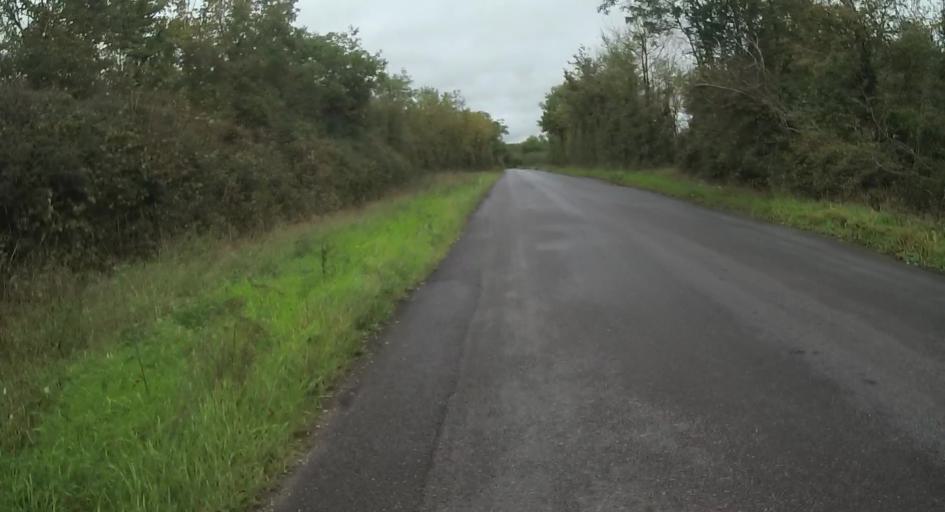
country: GB
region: England
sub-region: Hampshire
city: Tadley
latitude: 51.3850
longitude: -1.1805
